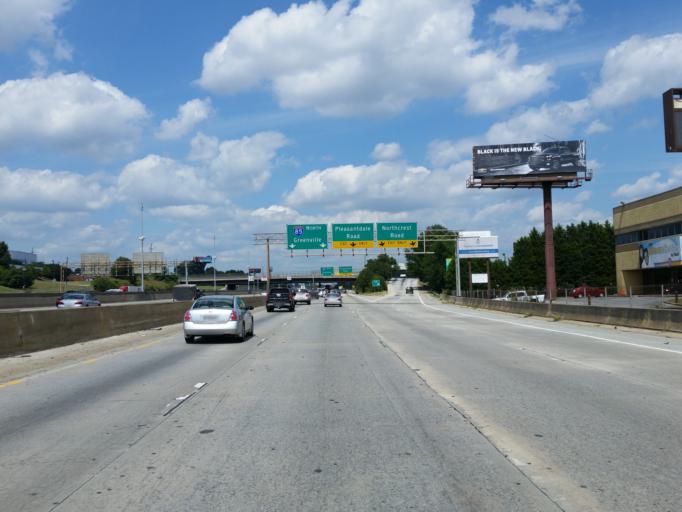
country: US
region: Georgia
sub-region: DeKalb County
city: Doraville
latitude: 33.8948
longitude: -84.2539
